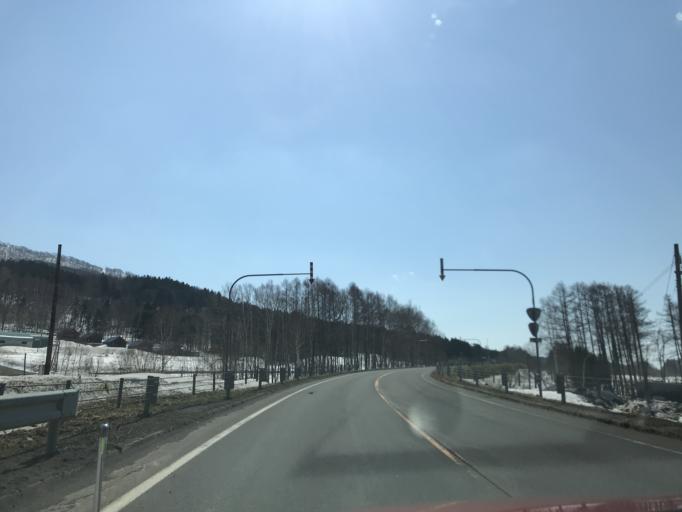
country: JP
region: Hokkaido
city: Nayoro
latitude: 44.7228
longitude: 142.2691
